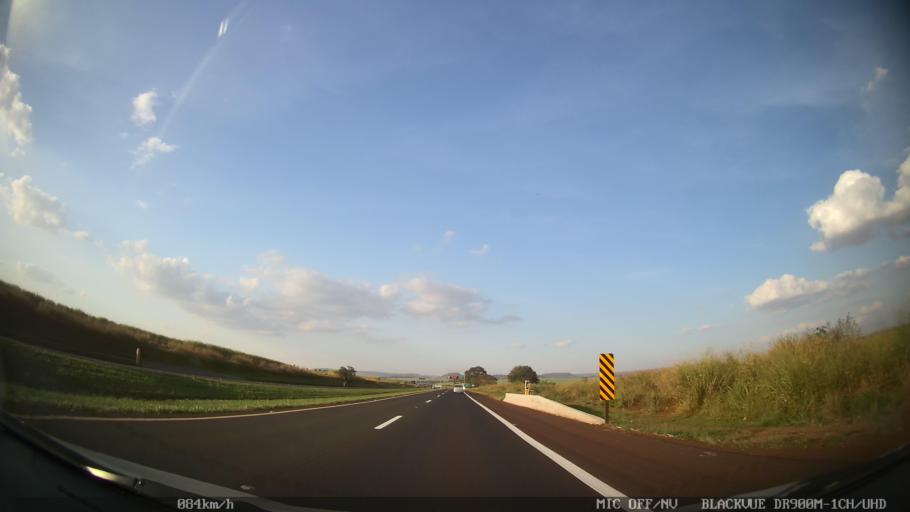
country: BR
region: Sao Paulo
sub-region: Ribeirao Preto
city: Ribeirao Preto
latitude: -21.1105
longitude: -47.7746
